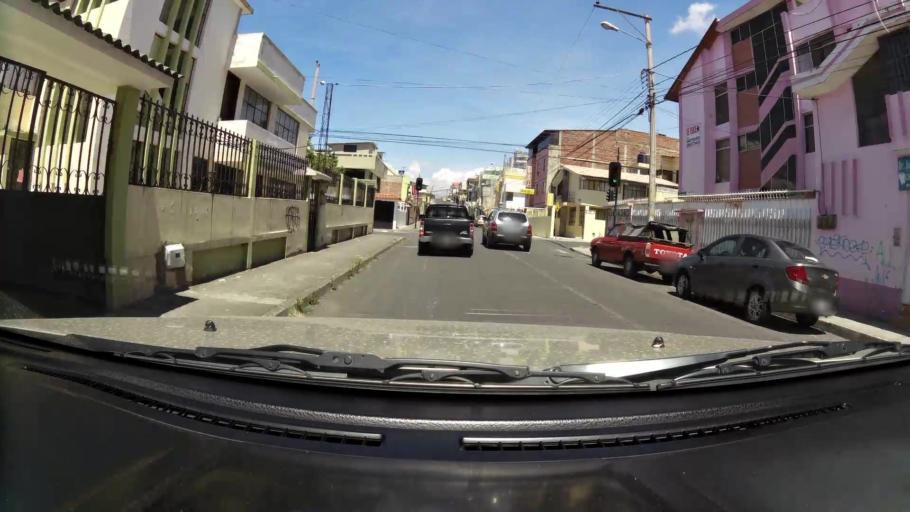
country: EC
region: Chimborazo
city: Riobamba
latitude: -1.6644
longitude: -78.6562
